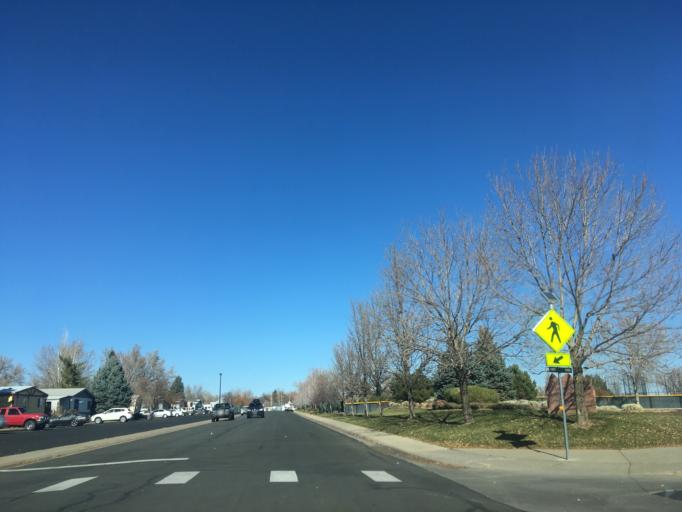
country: US
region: Colorado
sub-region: Boulder County
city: Lafayette
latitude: 39.9913
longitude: -105.0811
